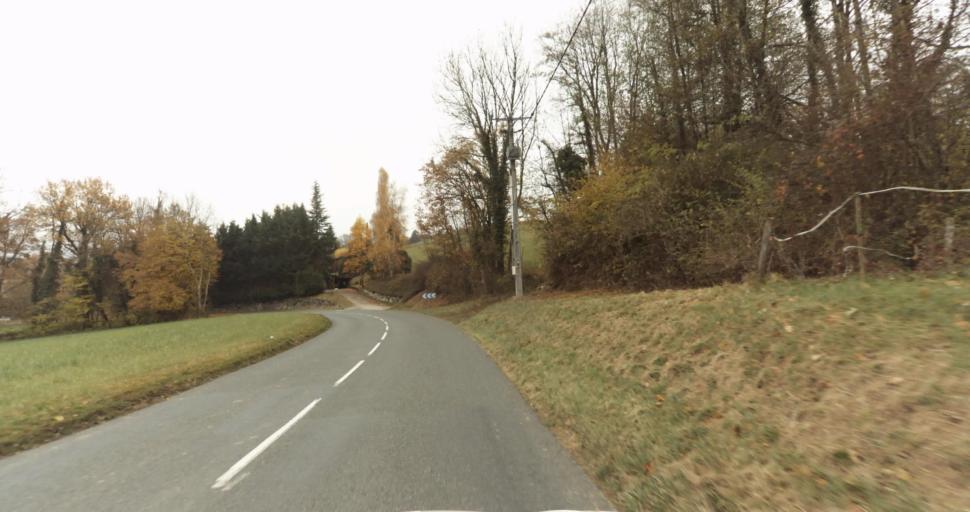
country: FR
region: Rhone-Alpes
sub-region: Departement de la Haute-Savoie
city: Cusy
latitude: 45.7804
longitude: 6.0153
